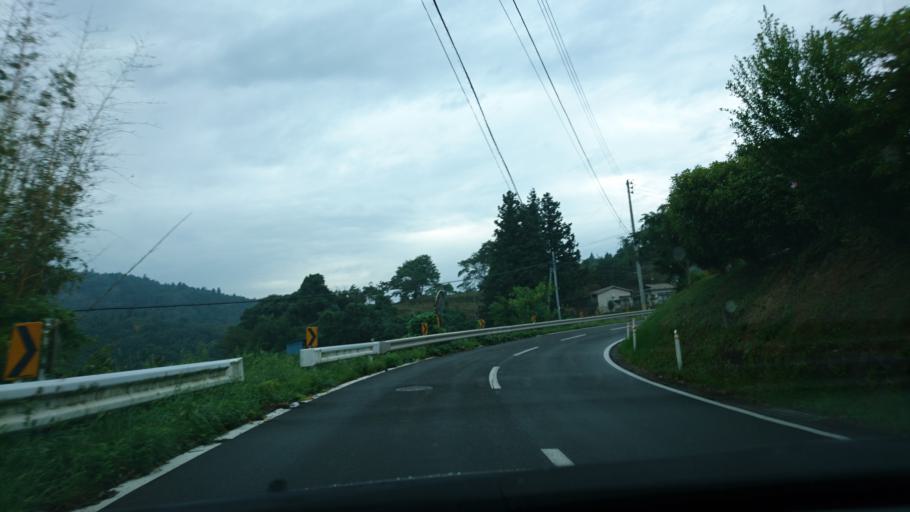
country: JP
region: Iwate
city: Ichinoseki
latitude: 38.9505
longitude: 141.2519
